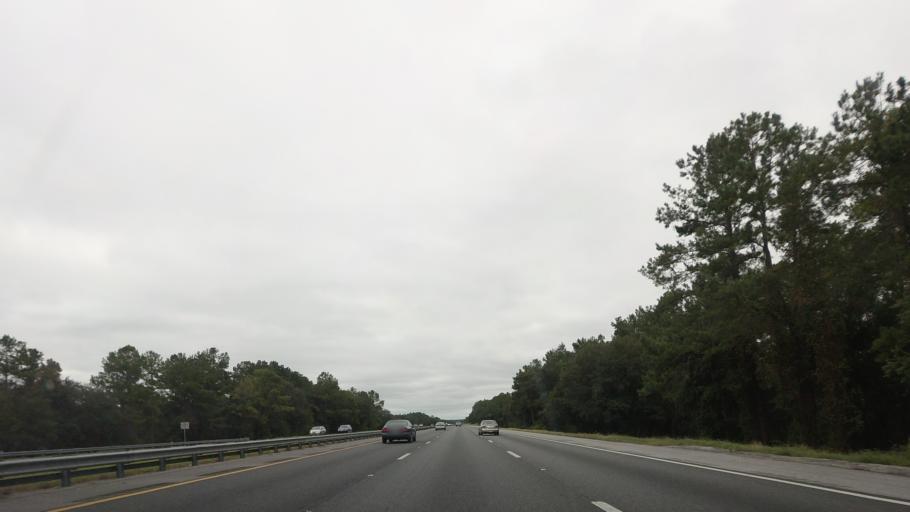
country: US
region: Florida
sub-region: Suwannee County
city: Wellborn
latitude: 30.3407
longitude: -82.8285
